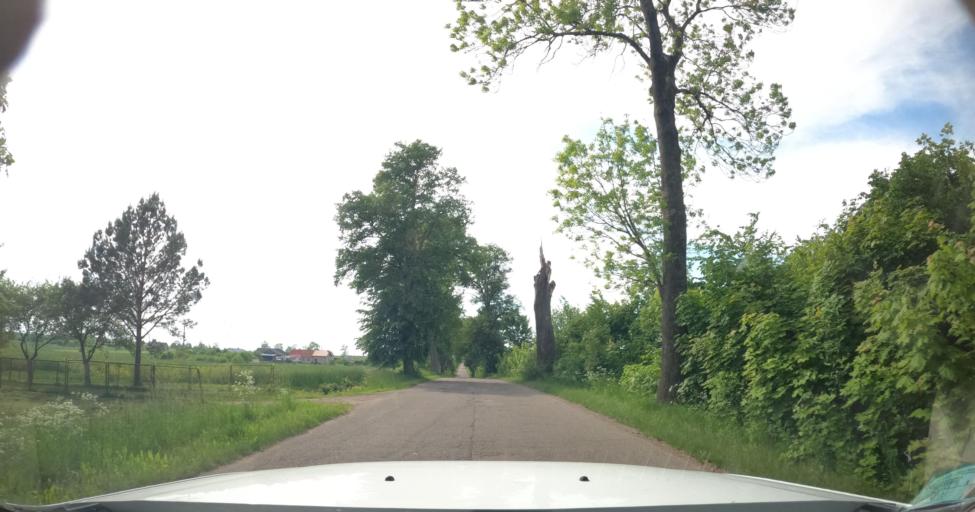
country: PL
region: Warmian-Masurian Voivodeship
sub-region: Powiat ostrodzki
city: Milakowo
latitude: 54.0209
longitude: 20.0260
